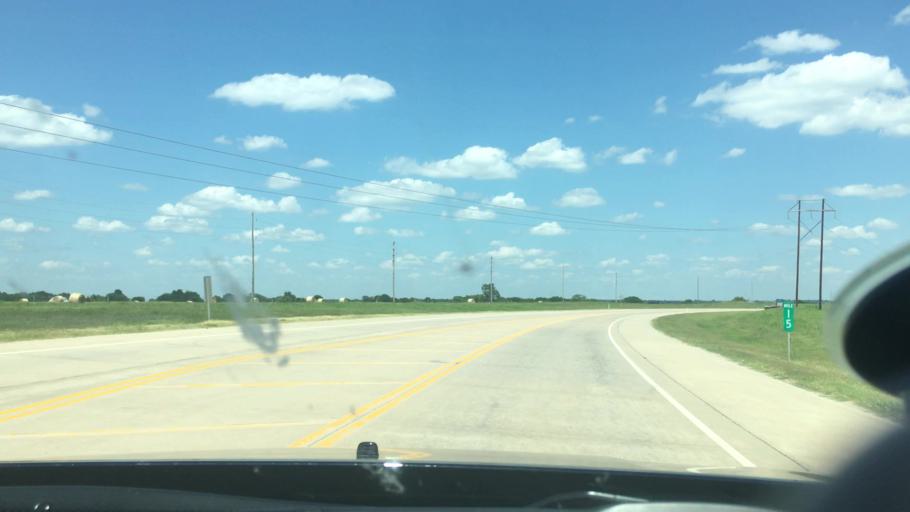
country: US
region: Oklahoma
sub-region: Garvin County
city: Stratford
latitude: 34.6506
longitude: -96.8350
